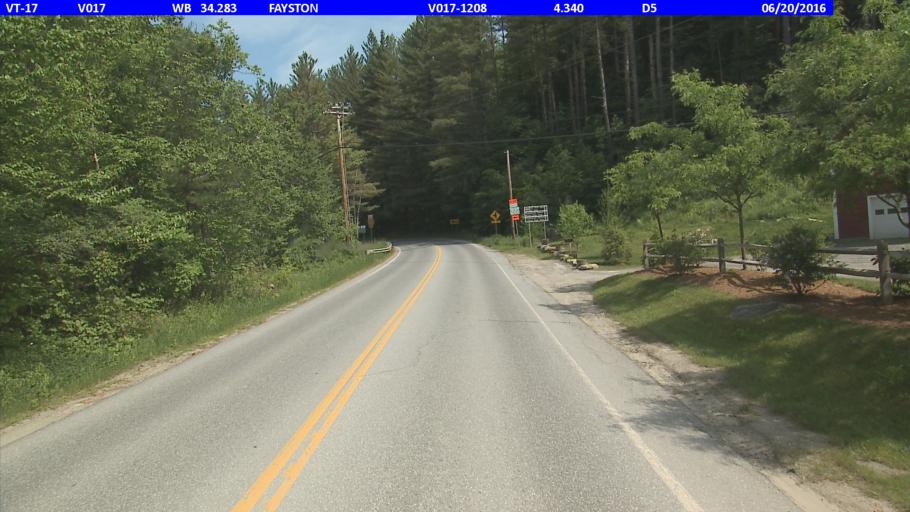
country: US
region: Vermont
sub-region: Washington County
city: Waterbury
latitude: 44.1844
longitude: -72.8711
